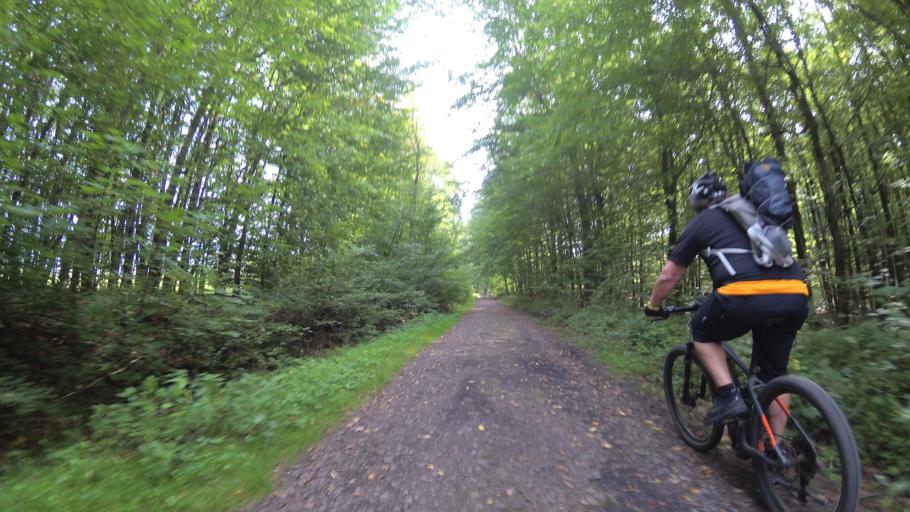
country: DE
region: Saarland
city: Friedrichsthal
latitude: 49.3042
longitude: 7.0948
